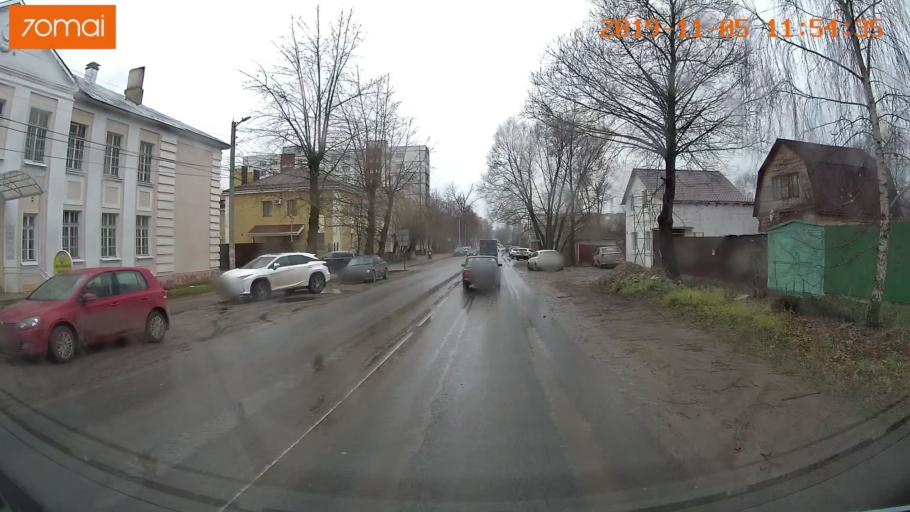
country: RU
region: Ivanovo
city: Bogorodskoye
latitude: 56.9900
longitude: 41.0313
